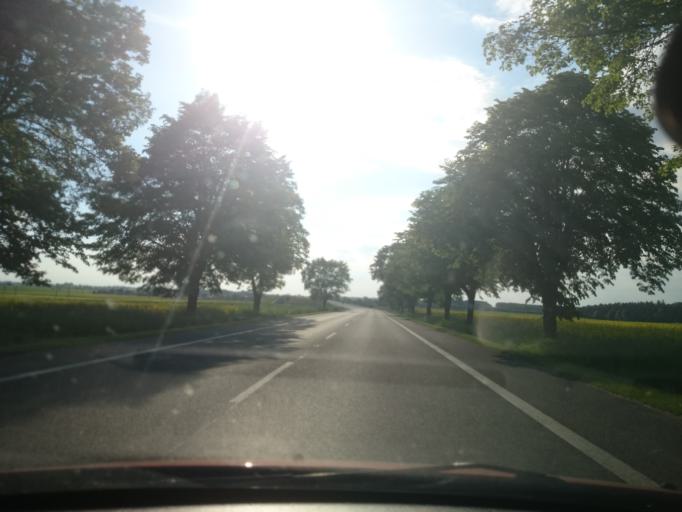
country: PL
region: Opole Voivodeship
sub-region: Powiat strzelecki
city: Jemielnica
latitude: 50.4912
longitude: 18.3945
